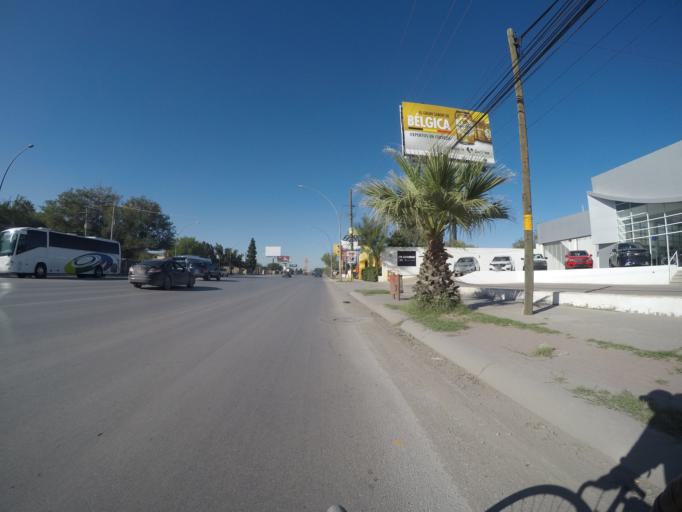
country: MX
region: Chihuahua
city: Ciudad Juarez
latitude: 31.7277
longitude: -106.4243
